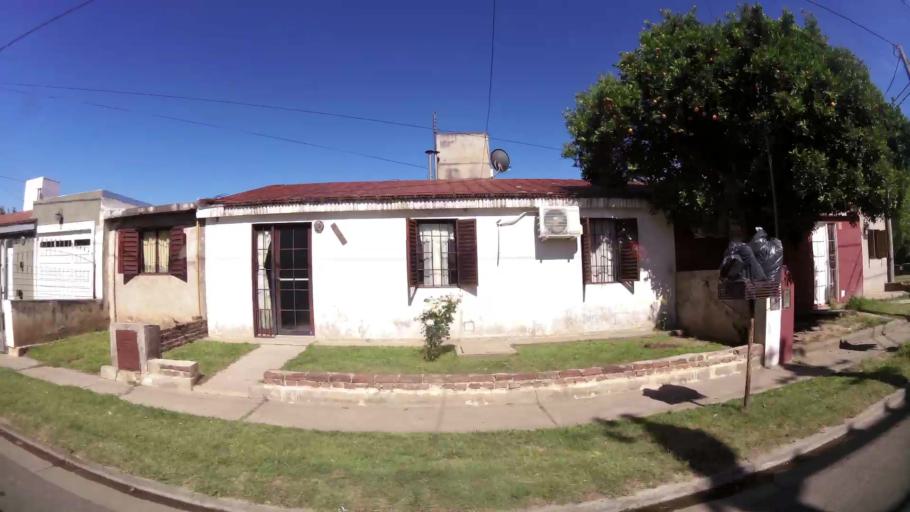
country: AR
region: Cordoba
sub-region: Departamento de Capital
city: Cordoba
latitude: -31.4370
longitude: -64.1379
